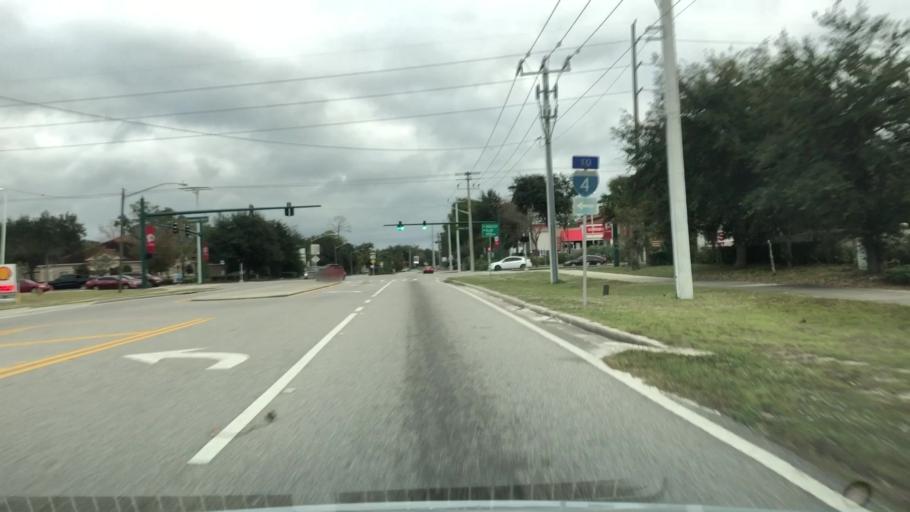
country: US
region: Florida
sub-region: Volusia County
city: Lake Helen
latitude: 28.9252
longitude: -81.1916
